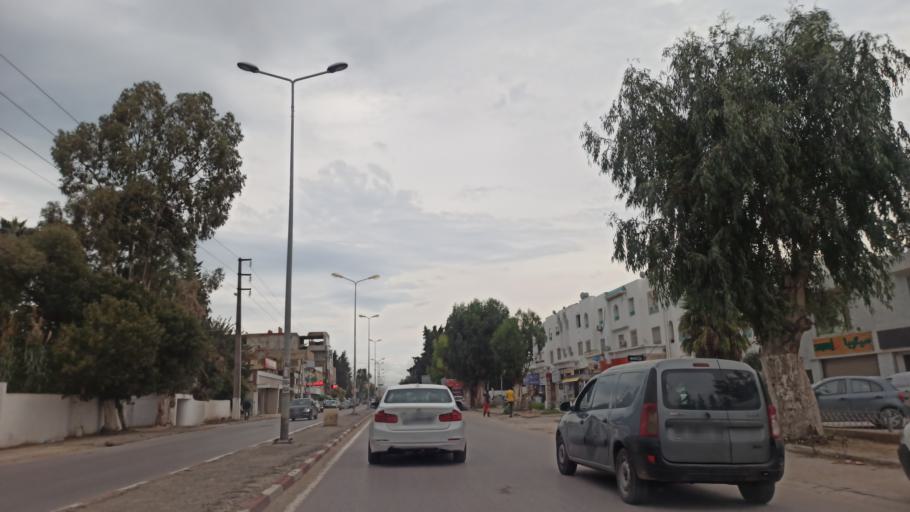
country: TN
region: Ariana
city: Ariana
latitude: 36.8709
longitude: 10.2484
